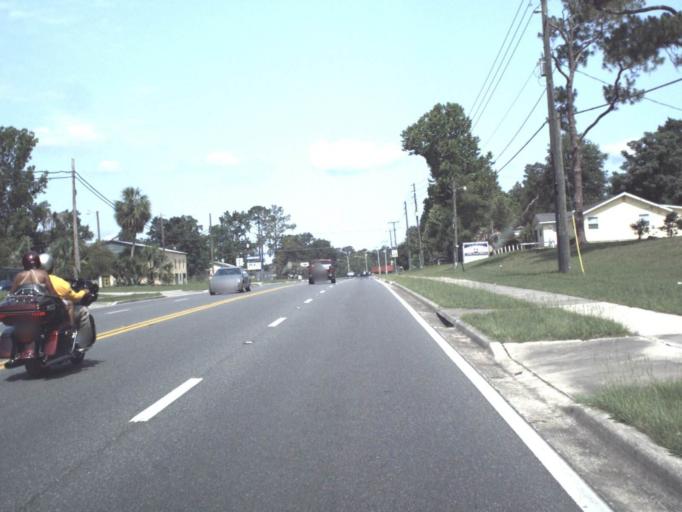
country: US
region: Florida
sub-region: Columbia County
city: Watertown
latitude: 30.1887
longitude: -82.6148
